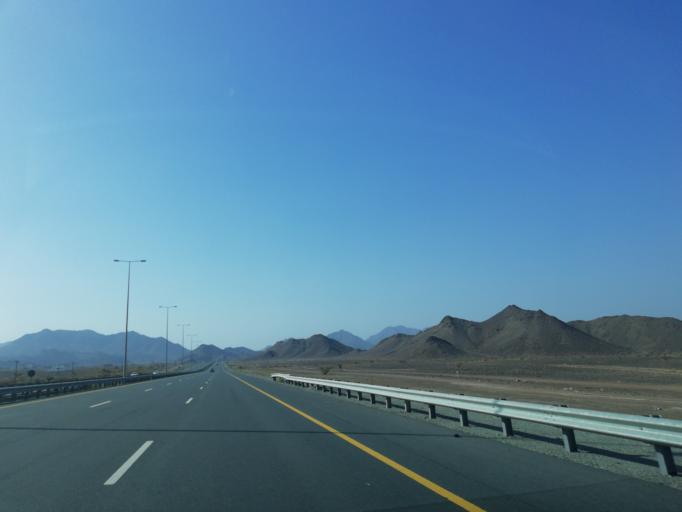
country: OM
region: Ash Sharqiyah
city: Ibra'
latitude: 22.9386
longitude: 58.2515
